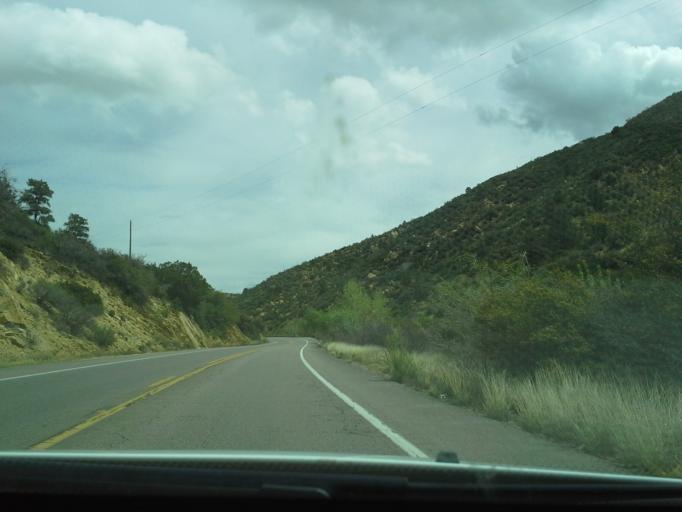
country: US
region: Arizona
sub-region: Gila County
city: Miami
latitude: 33.3774
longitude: -110.9106
